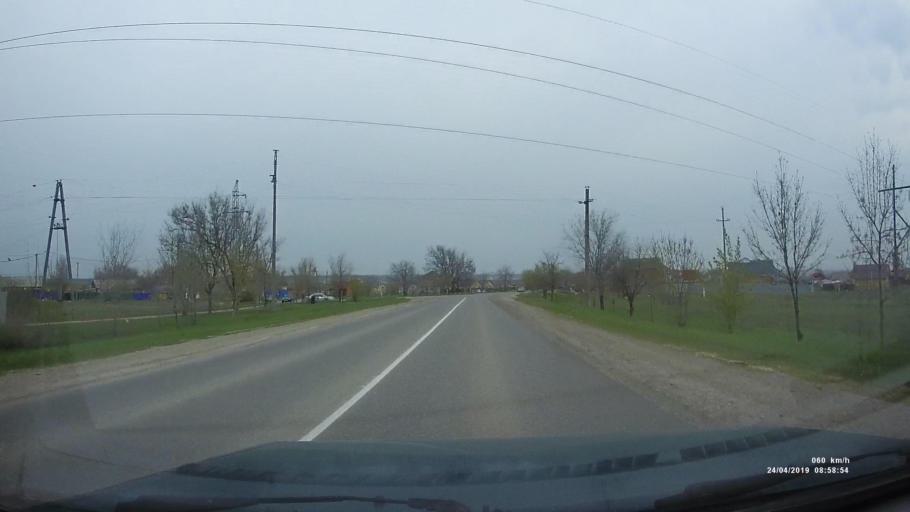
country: RU
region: Kalmykiya
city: Arshan'
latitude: 46.3110
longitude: 44.2027
